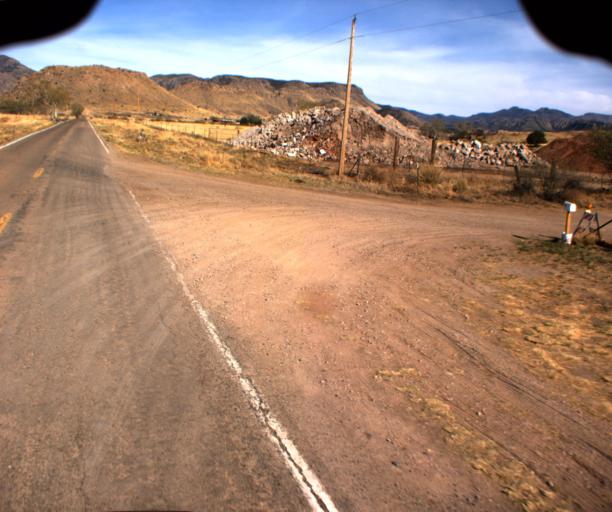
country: US
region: Arizona
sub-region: Cochise County
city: Willcox
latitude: 32.0067
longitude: -109.4056
